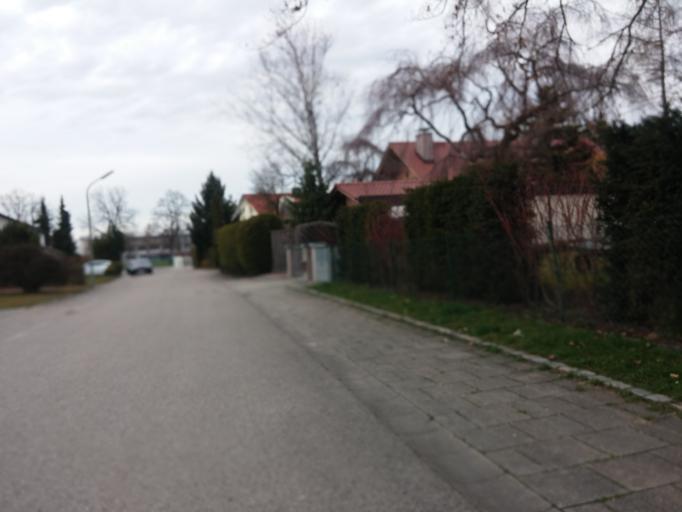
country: DE
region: Bavaria
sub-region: Upper Bavaria
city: Vaterstetten
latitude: 48.0916
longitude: 11.7602
